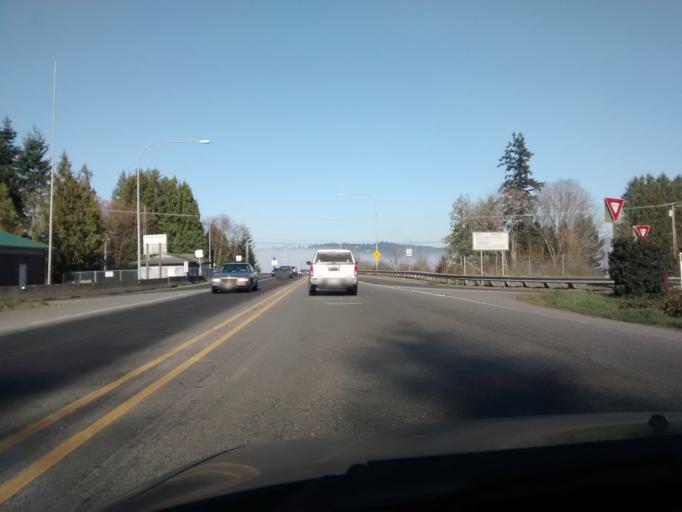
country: US
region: Washington
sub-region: Kitsap County
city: Lofall
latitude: 47.8517
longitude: -122.6100
